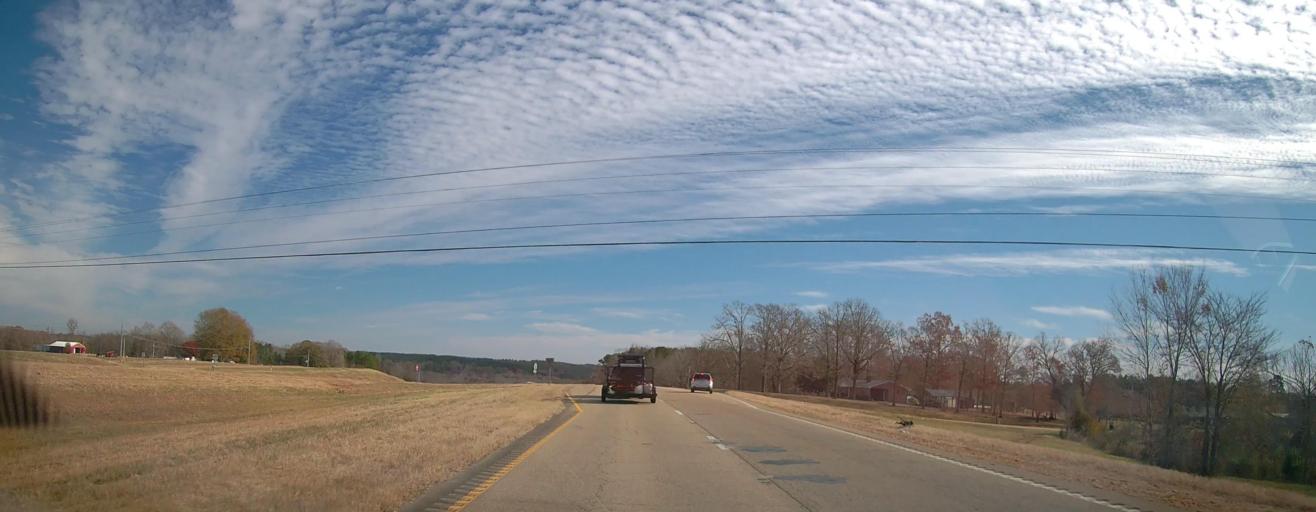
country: US
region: Mississippi
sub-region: Tippah County
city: Ripley
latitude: 34.9464
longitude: -88.8019
